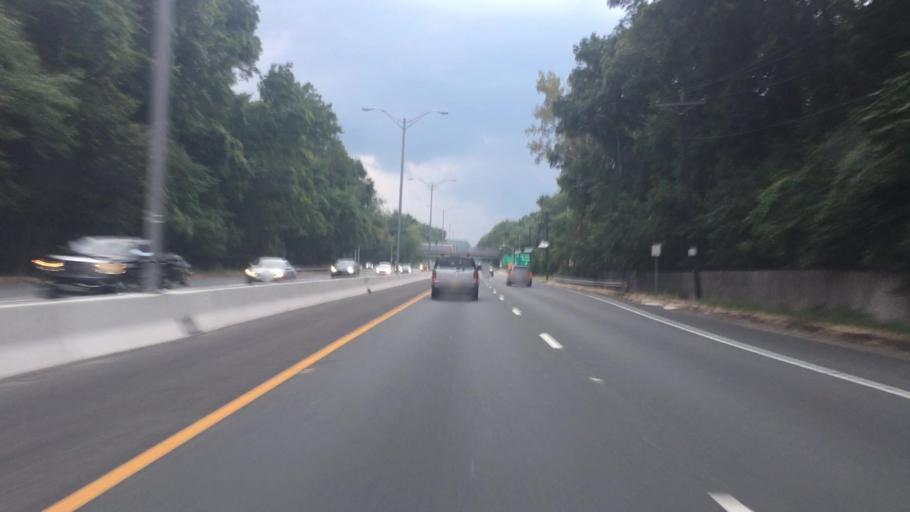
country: US
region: New Jersey
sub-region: Bergen County
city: Midland Park
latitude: 40.9849
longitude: -74.1650
